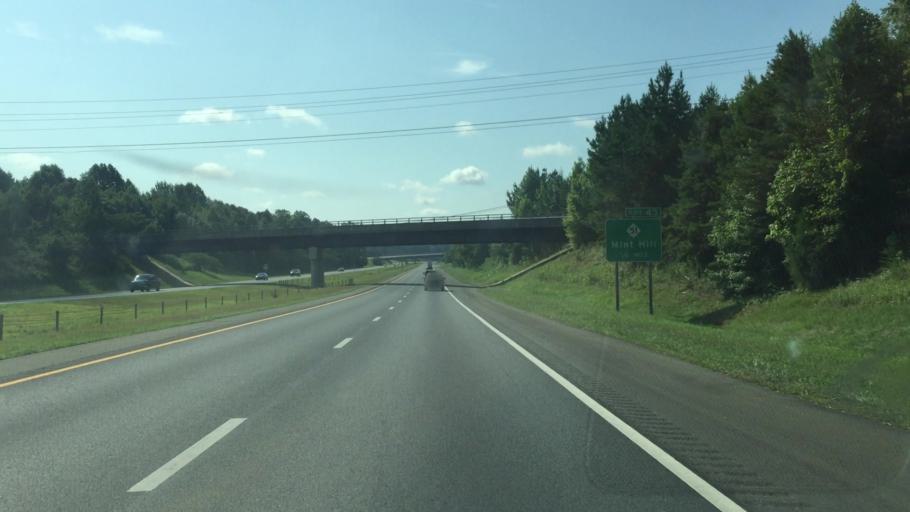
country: US
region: North Carolina
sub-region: Mecklenburg County
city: Mint Hill
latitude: 35.2093
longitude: -80.6409
